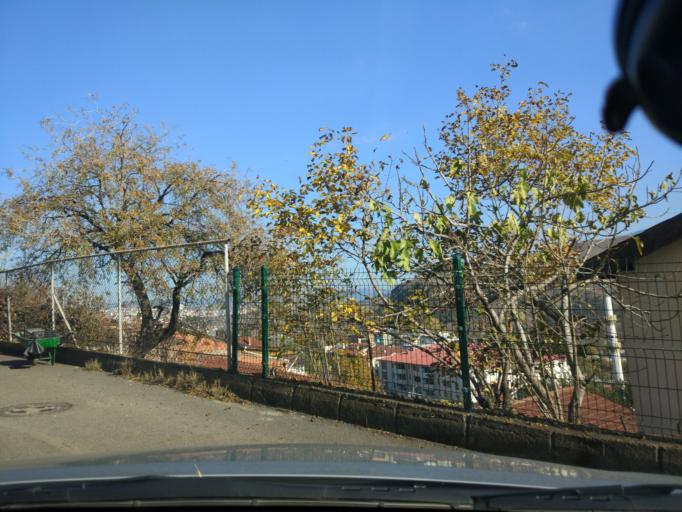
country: TR
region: Karabuk
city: Karabuk
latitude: 41.2035
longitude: 32.6276
